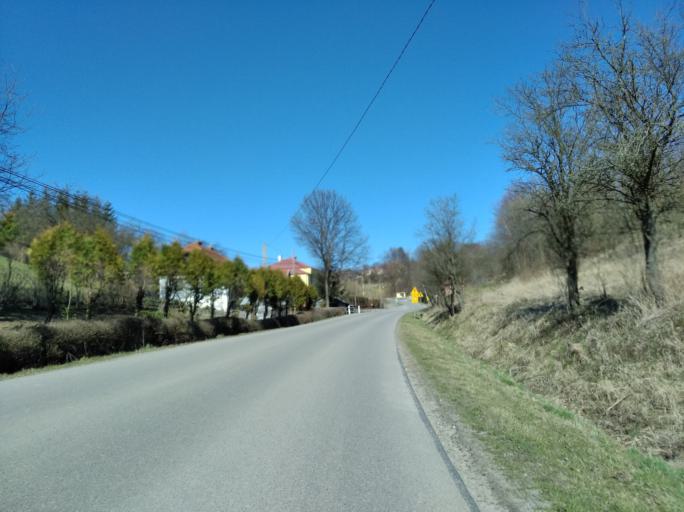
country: PL
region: Subcarpathian Voivodeship
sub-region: Powiat strzyzowski
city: Wisniowa
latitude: 49.8936
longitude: 21.6645
